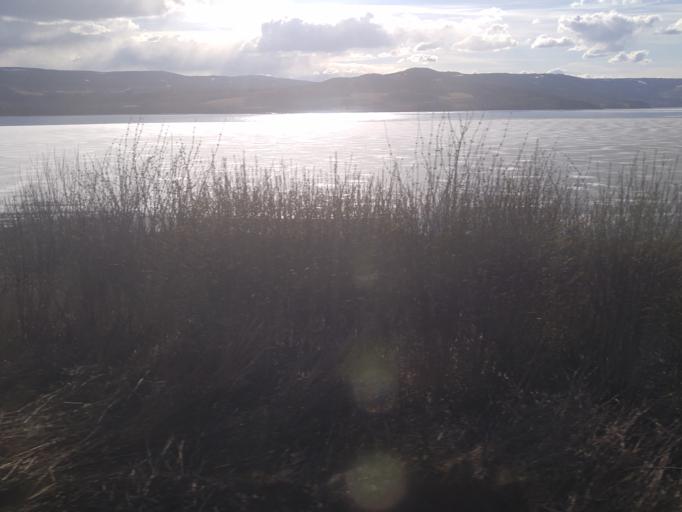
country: NO
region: Hedmark
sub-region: Ringsaker
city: Moelv
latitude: 60.9765
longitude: 10.6527
